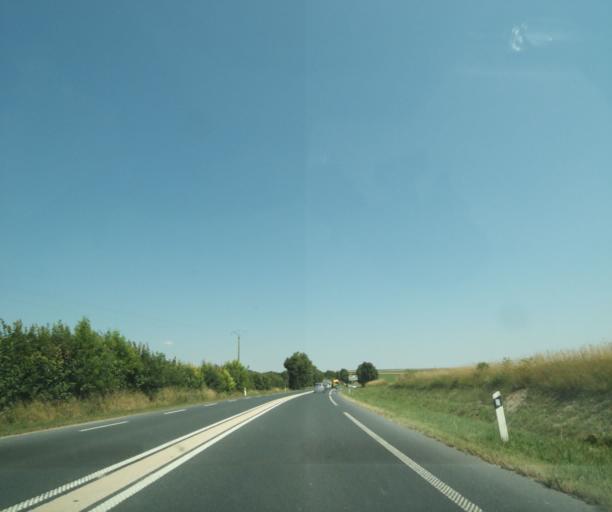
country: FR
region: Champagne-Ardenne
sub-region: Departement de la Marne
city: Mourmelon-le-Grand
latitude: 49.0615
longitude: 4.2971
